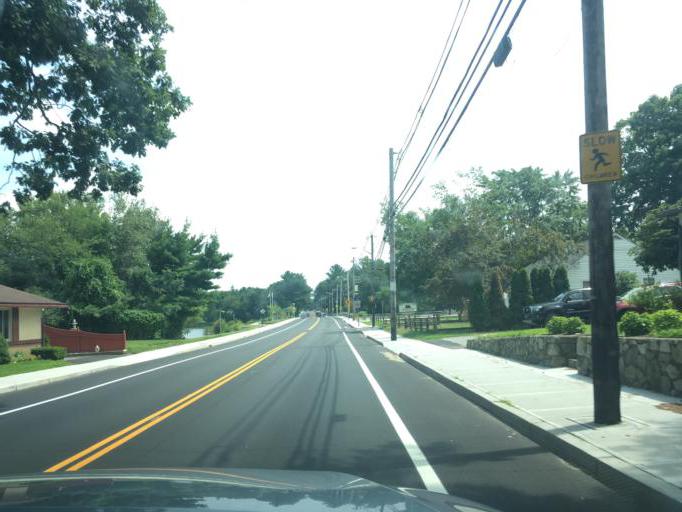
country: US
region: Rhode Island
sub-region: Kent County
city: West Warwick
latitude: 41.6794
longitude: -71.5574
